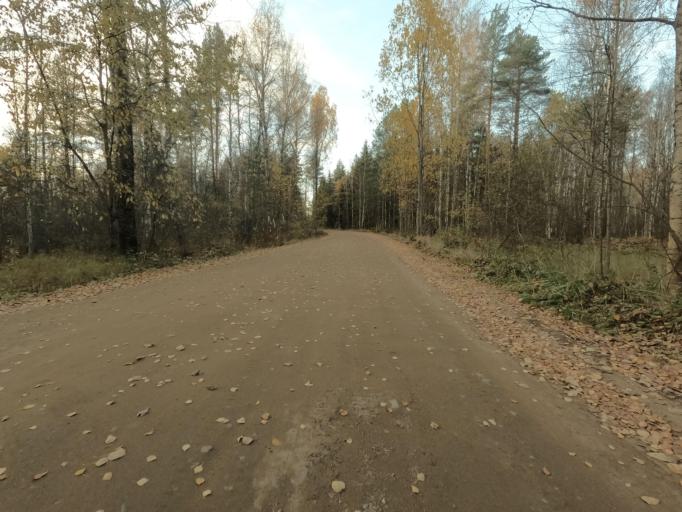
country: RU
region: Leningrad
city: Priladozhskiy
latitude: 59.7452
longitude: 31.3082
